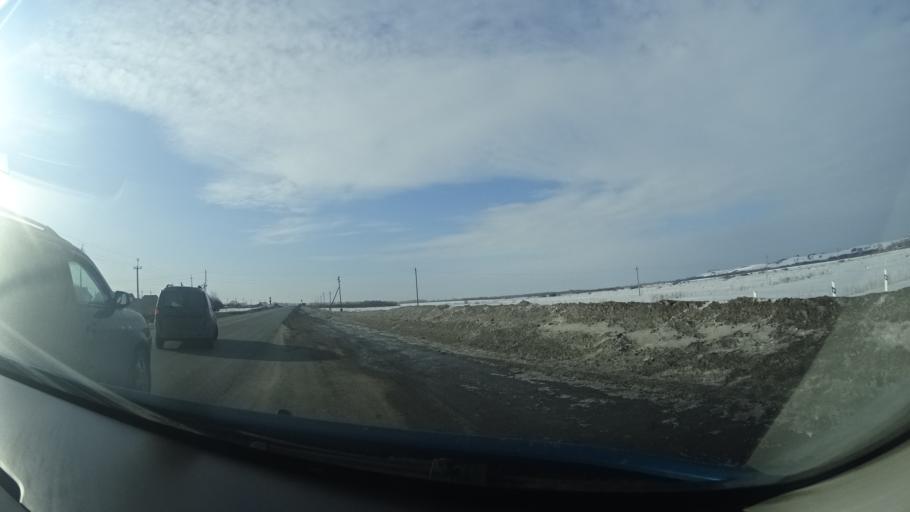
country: RU
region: Perm
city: Kuyeda
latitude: 56.4389
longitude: 55.5739
